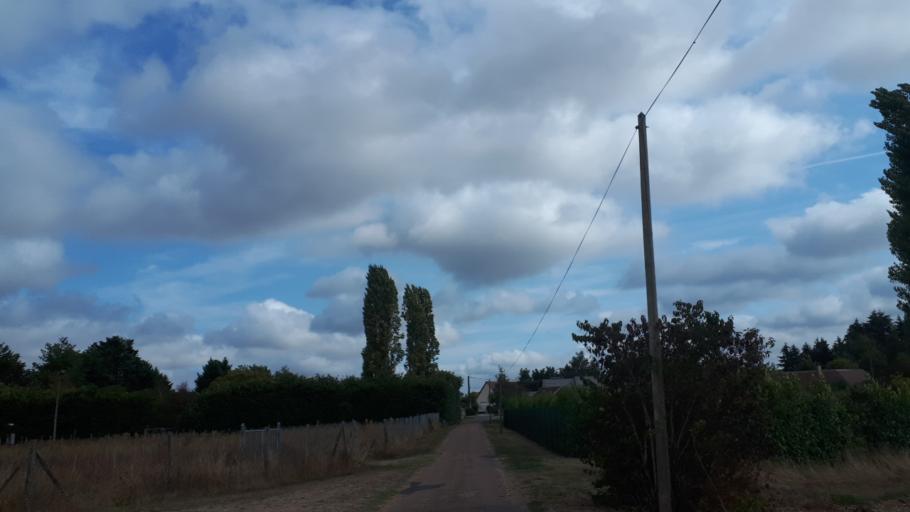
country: FR
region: Centre
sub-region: Departement du Loir-et-Cher
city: Villiers-sur-Loir
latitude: 47.7917
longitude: 0.9955
